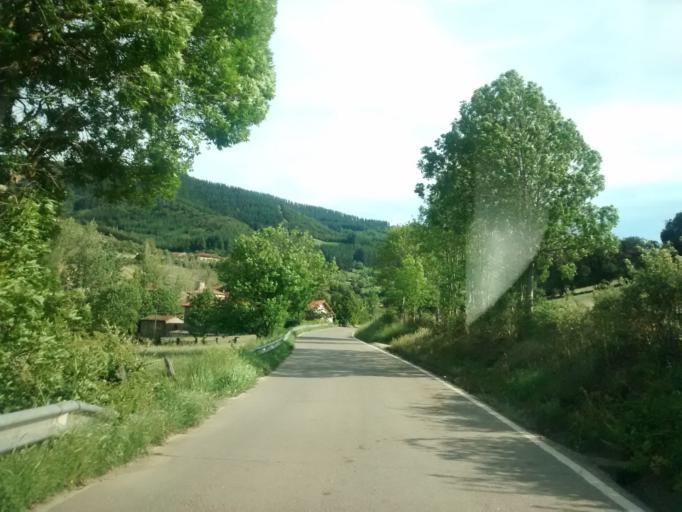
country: ES
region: Cantabria
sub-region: Provincia de Cantabria
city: Potes
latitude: 43.1779
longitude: -4.6024
